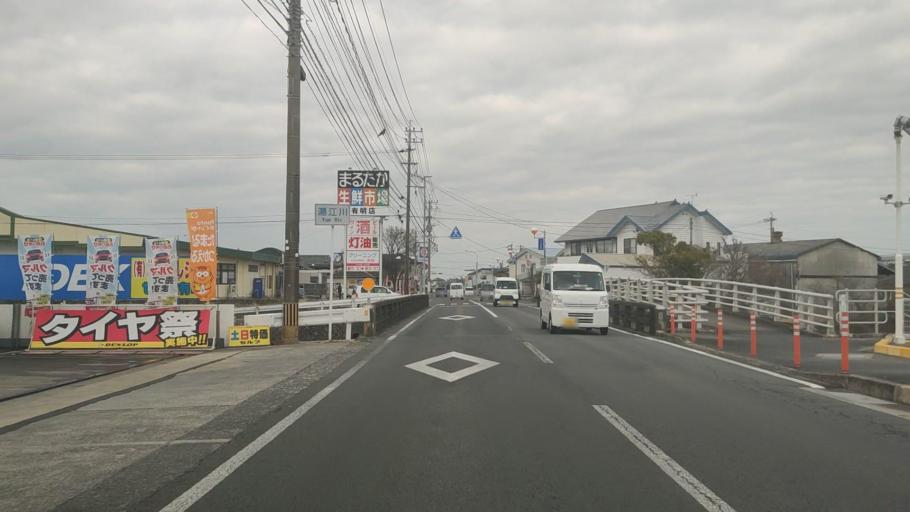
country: JP
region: Nagasaki
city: Shimabara
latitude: 32.8609
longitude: 130.3261
